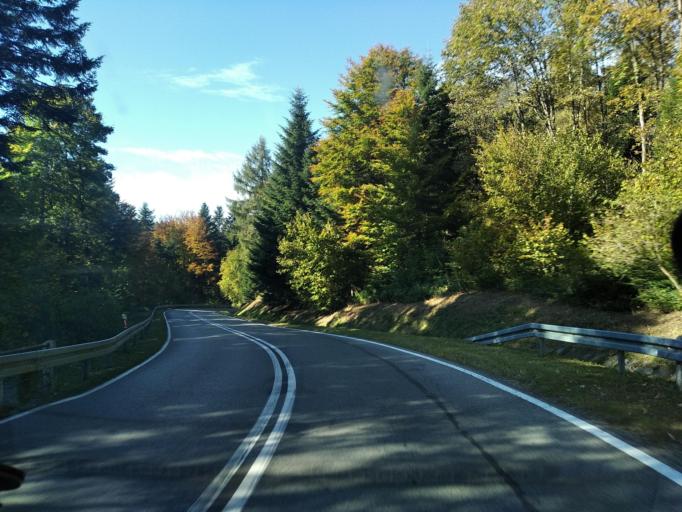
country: PL
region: Subcarpathian Voivodeship
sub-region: Powiat leski
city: Cisna
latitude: 49.2449
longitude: 22.2911
